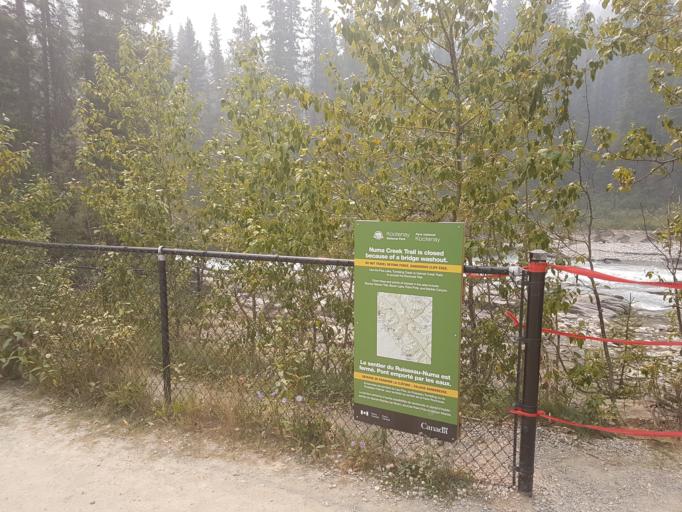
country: CA
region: Alberta
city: Lake Louise
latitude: 51.1328
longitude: -116.1322
